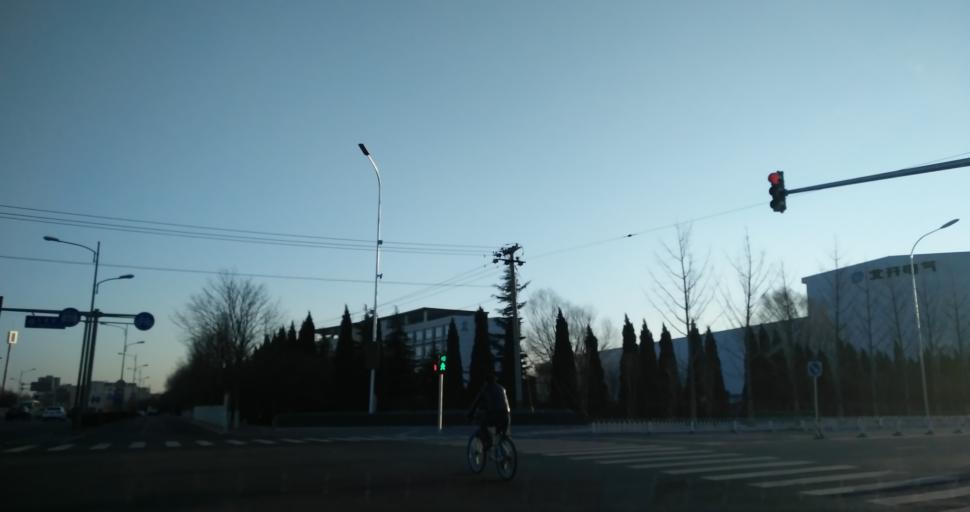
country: CN
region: Beijing
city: Jiugong
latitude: 39.7790
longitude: 116.5236
